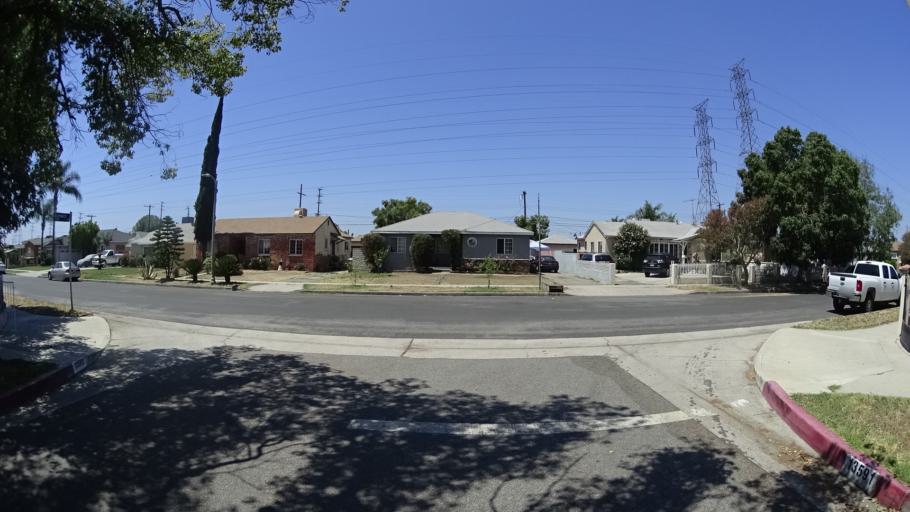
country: US
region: California
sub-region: Los Angeles County
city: San Fernando
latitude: 34.2356
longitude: -118.4293
